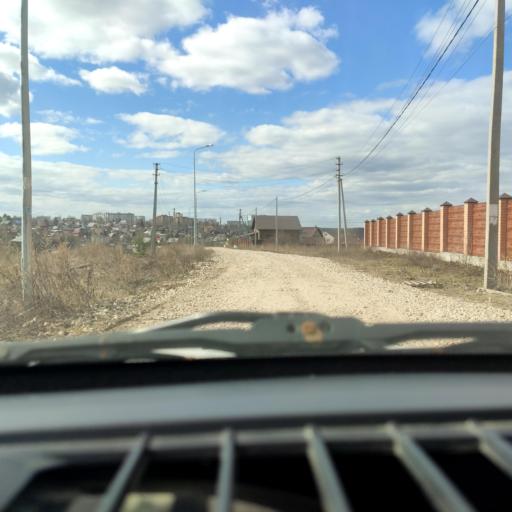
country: RU
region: Perm
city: Perm
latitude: 58.0244
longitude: 56.3499
